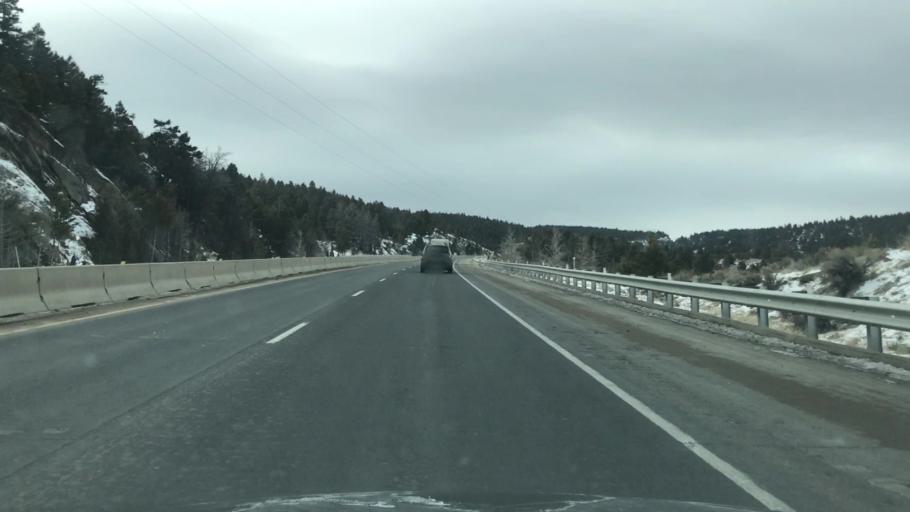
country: US
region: Montana
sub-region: Jefferson County
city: Whitehall
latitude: 45.9117
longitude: -112.3007
